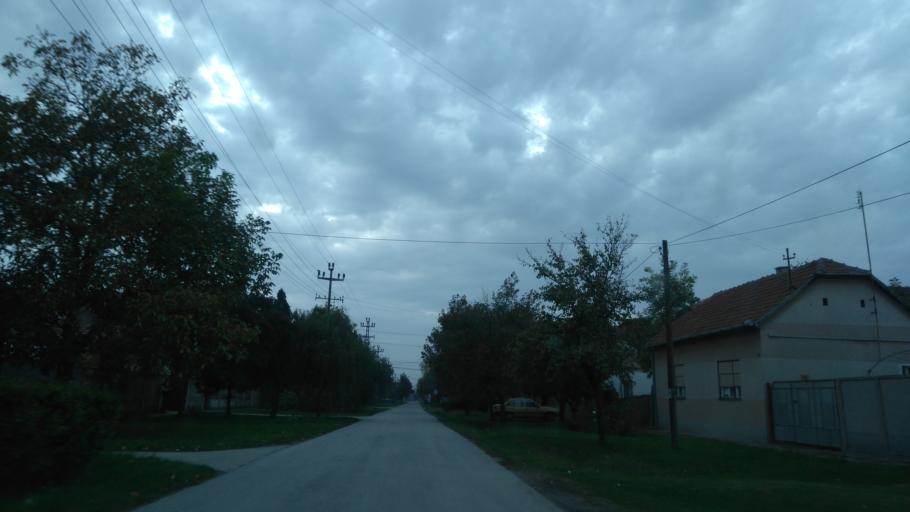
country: RS
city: Mol
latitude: 45.7652
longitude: 20.1335
